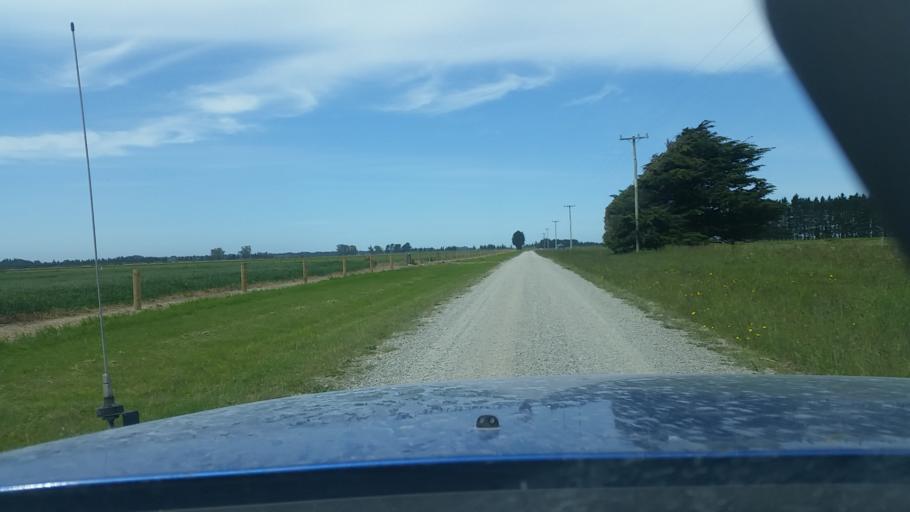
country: NZ
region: Canterbury
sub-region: Ashburton District
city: Tinwald
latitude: -44.0561
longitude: 171.7744
